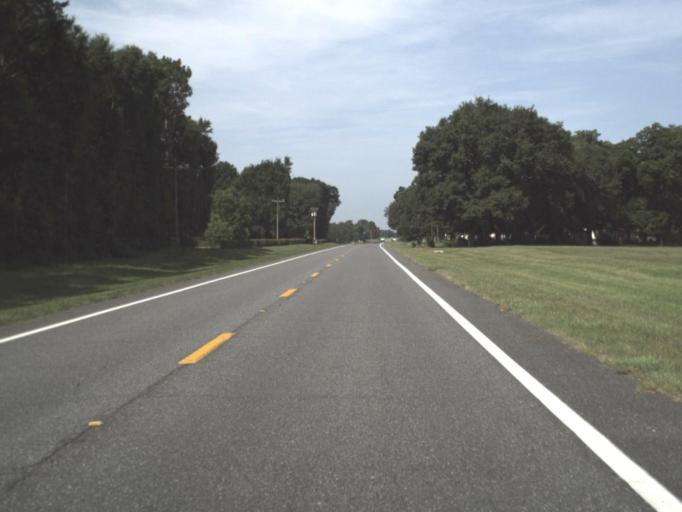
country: US
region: Florida
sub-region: Lafayette County
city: Mayo
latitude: 30.1939
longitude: -83.1161
